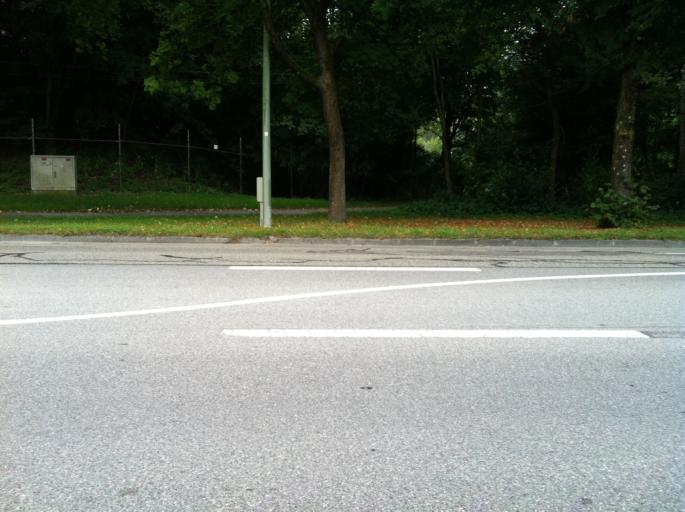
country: DE
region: Bavaria
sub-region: Upper Bavaria
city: Unterfoehring
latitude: 48.2107
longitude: 11.6335
